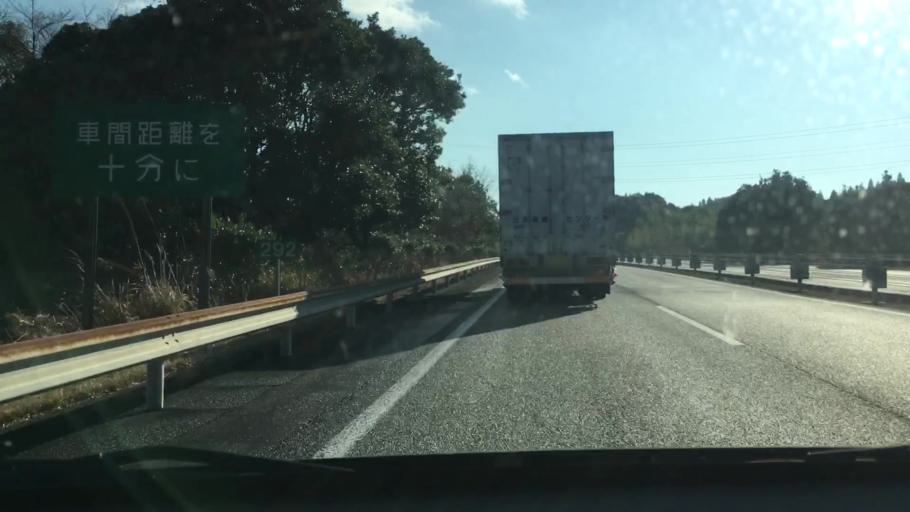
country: JP
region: Kagoshima
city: Okuchi-shinohara
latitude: 31.9328
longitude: 130.7064
